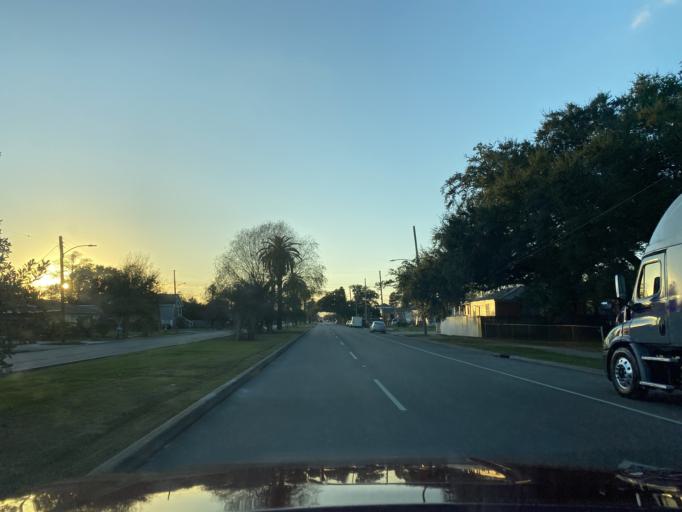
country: US
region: Louisiana
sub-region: Orleans Parish
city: New Orleans
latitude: 30.0223
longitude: -90.0566
